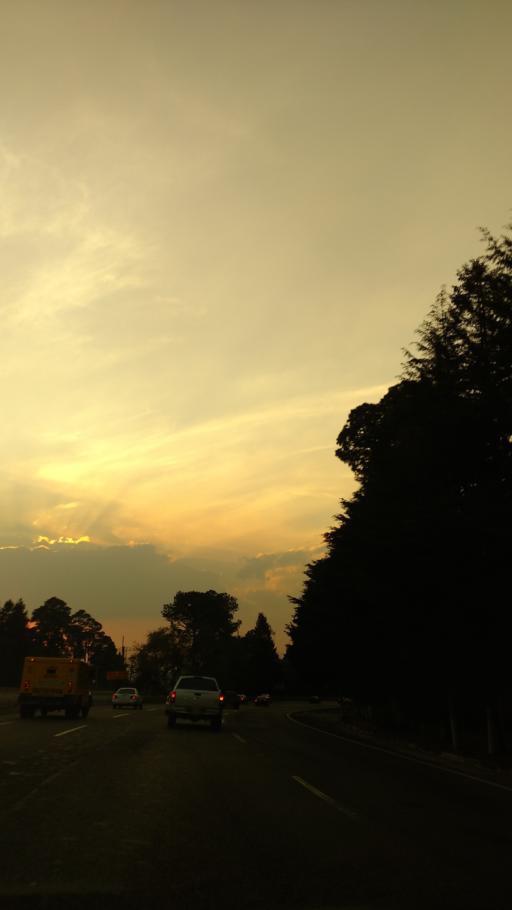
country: MX
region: Morelos
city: San Jeronimo Acazulco
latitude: 19.2978
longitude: -99.4055
